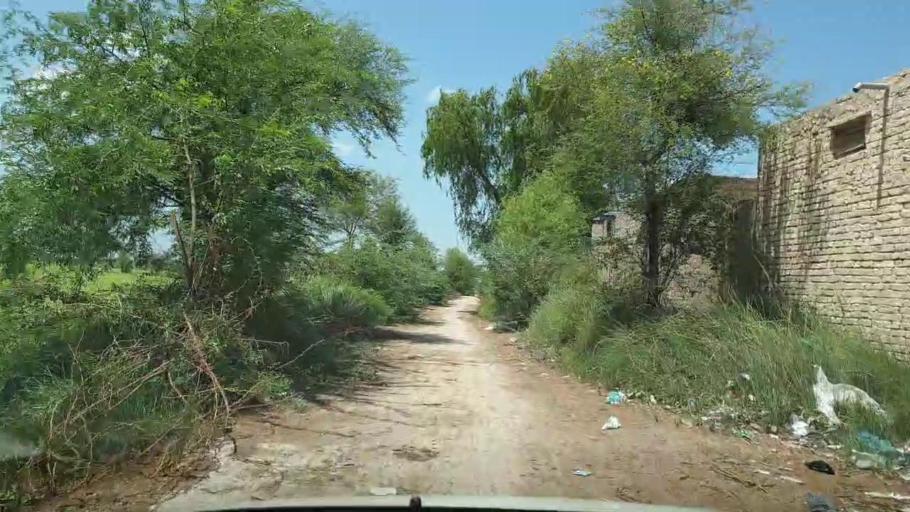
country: PK
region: Sindh
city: Sanghar
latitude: 26.0712
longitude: 69.0478
